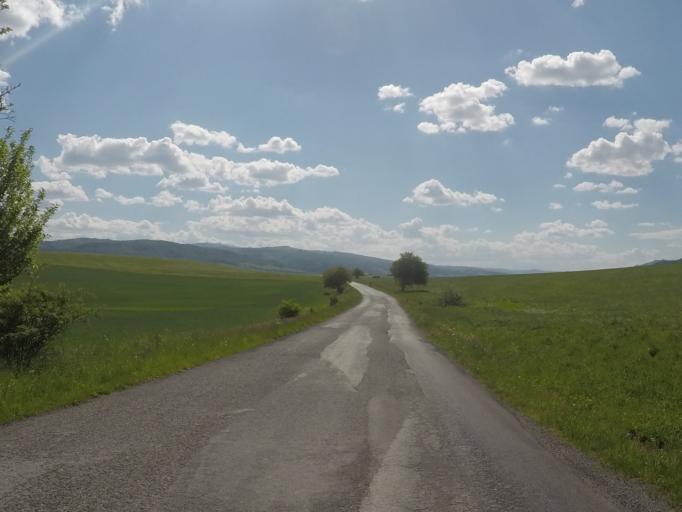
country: SK
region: Presovsky
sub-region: Okres Poprad
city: Poprad
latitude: 49.0023
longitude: 20.3744
